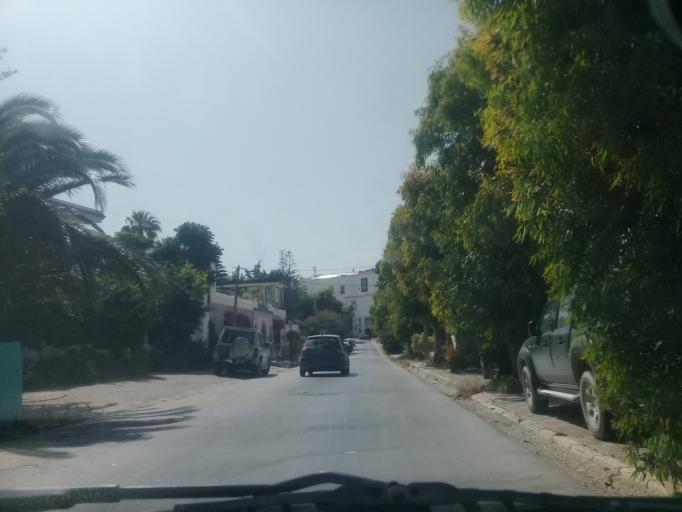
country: TN
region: Tunis
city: Al Marsa
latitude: 36.8830
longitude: 10.3360
